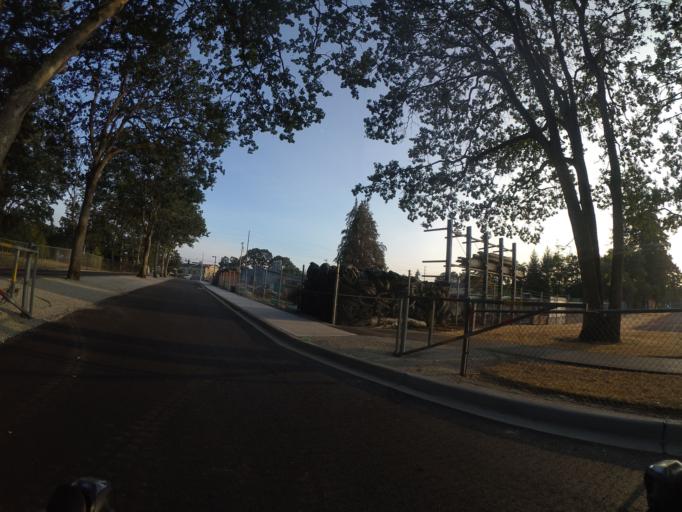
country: US
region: Washington
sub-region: Pierce County
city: Lakewood
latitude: 47.1774
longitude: -122.5104
